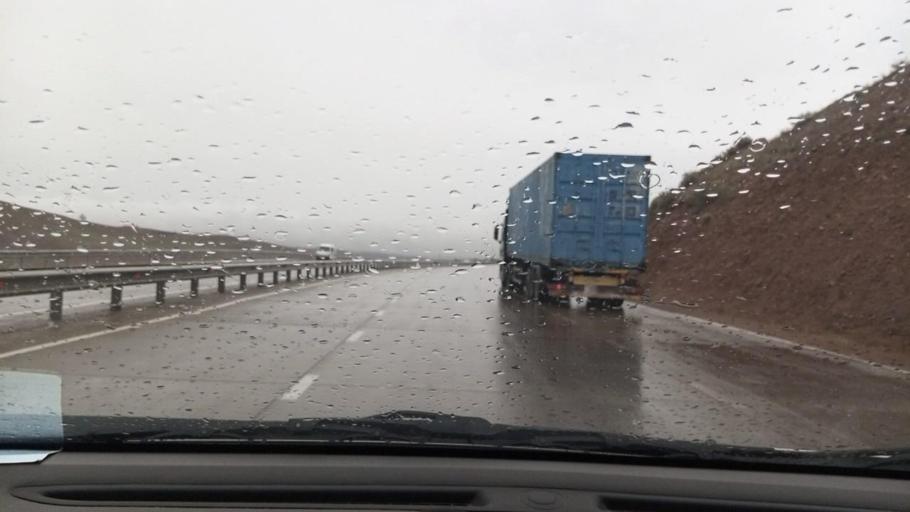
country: UZ
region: Namangan
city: Pop Shahri
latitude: 40.9286
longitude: 70.7132
